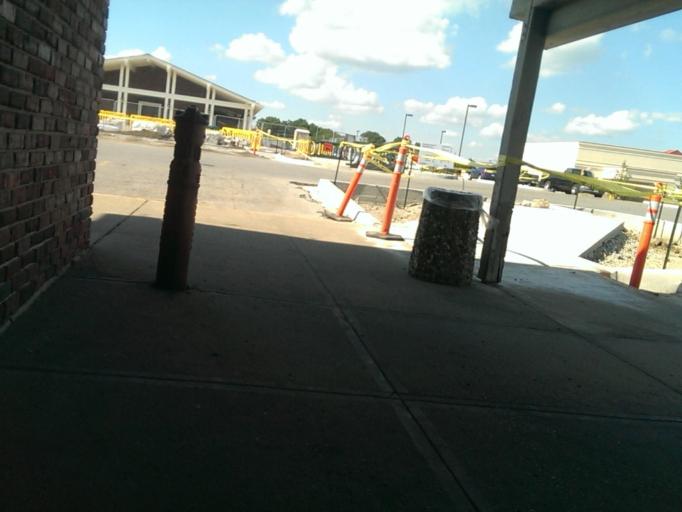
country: US
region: Kansas
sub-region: Johnson County
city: Leawood
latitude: 38.9238
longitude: -94.5853
